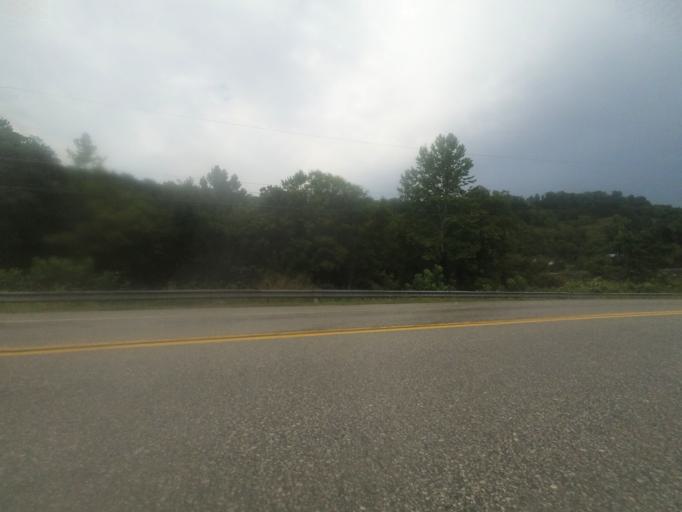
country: US
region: West Virginia
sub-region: Cabell County
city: Huntington
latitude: 38.3893
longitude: -82.3984
